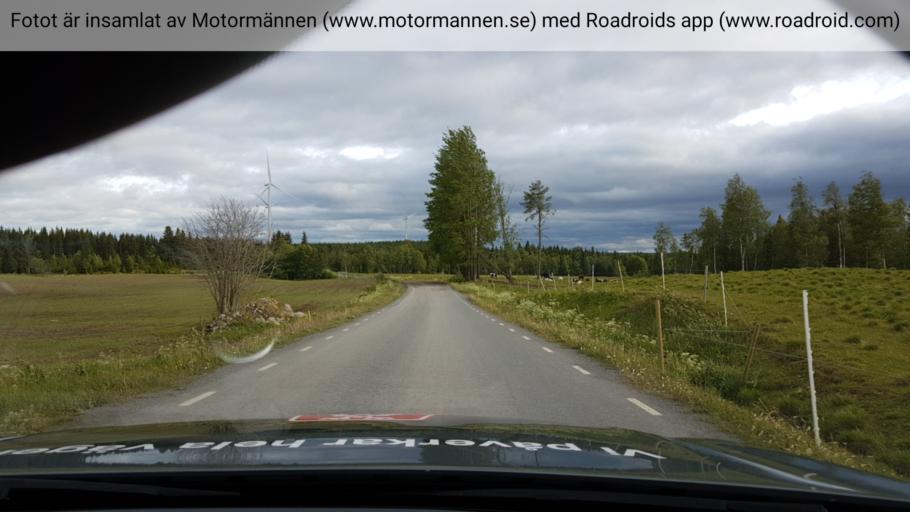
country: SE
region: Jaemtland
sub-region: OEstersunds Kommun
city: Lit
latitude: 63.6081
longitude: 14.9989
